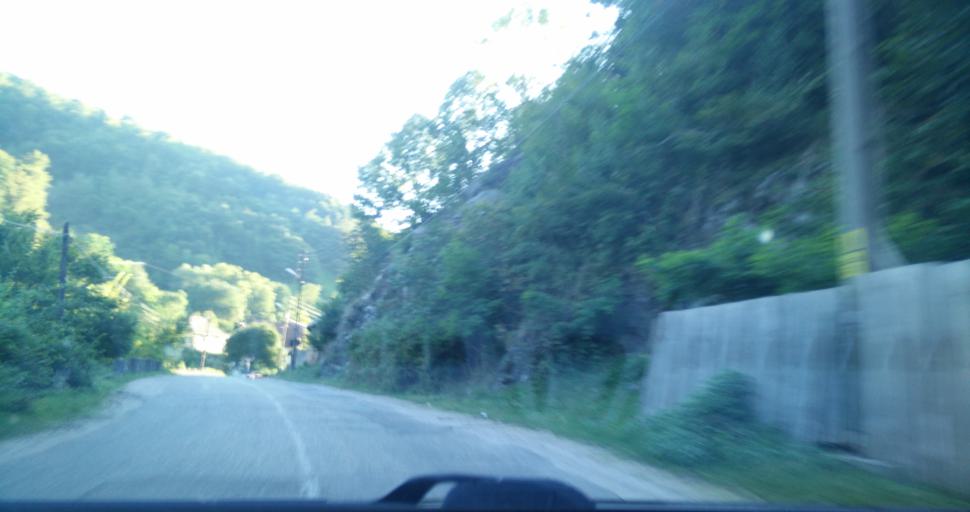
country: RO
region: Bihor
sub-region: Oras Nucet
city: Nucet
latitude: 46.4816
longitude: 22.5891
